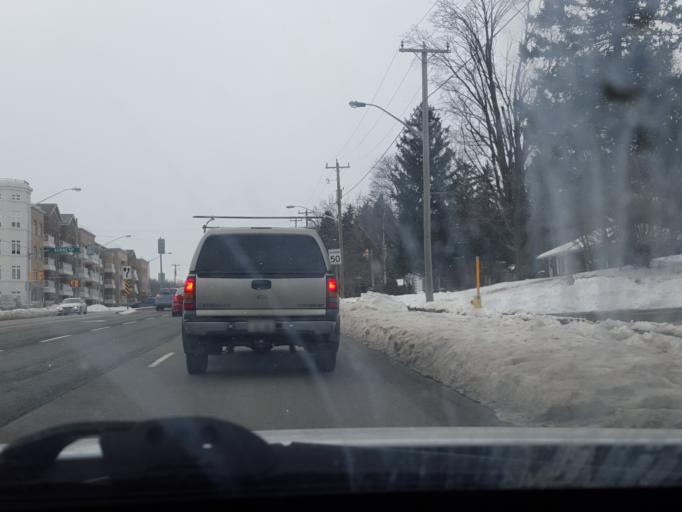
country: CA
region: Ontario
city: Vaughan
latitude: 43.9271
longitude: -79.5346
